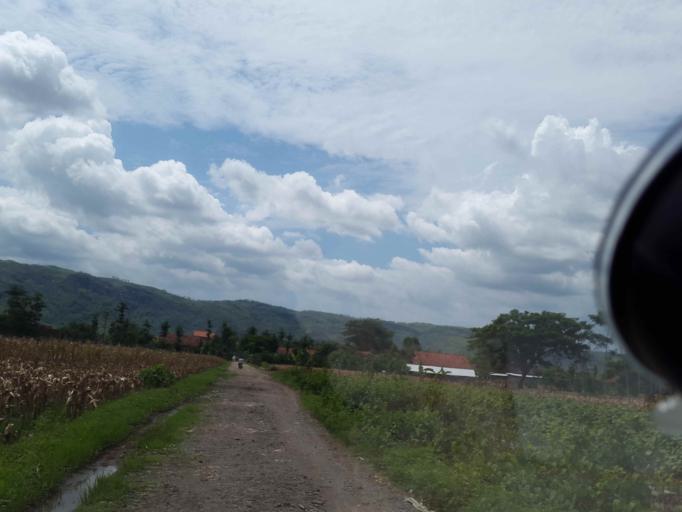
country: ID
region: East Java
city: Pojok
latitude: -8.1418
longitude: 111.8808
